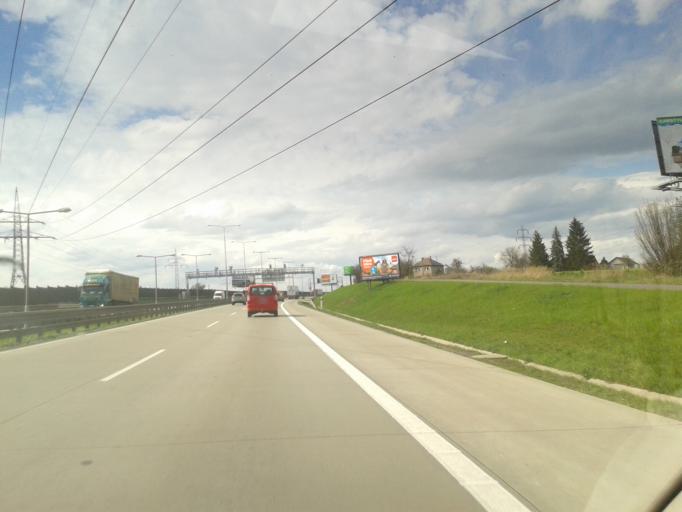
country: CZ
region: Central Bohemia
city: Rudna
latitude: 50.0342
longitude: 14.2779
